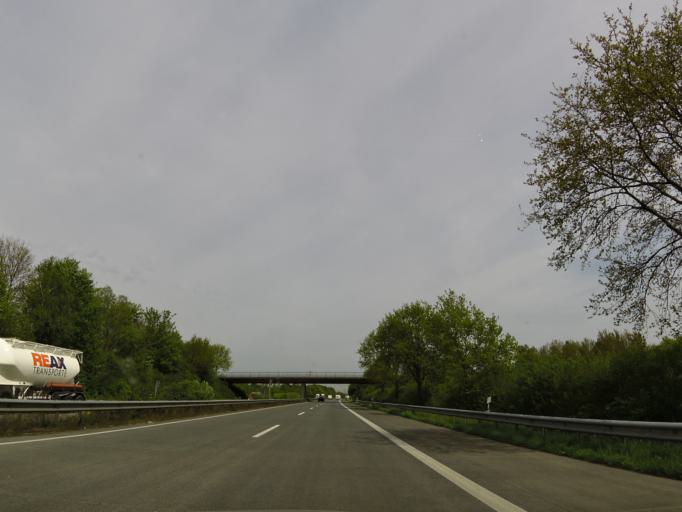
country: DE
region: Schleswig-Holstein
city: Kolln-Reisiek
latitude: 53.7549
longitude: 9.7091
